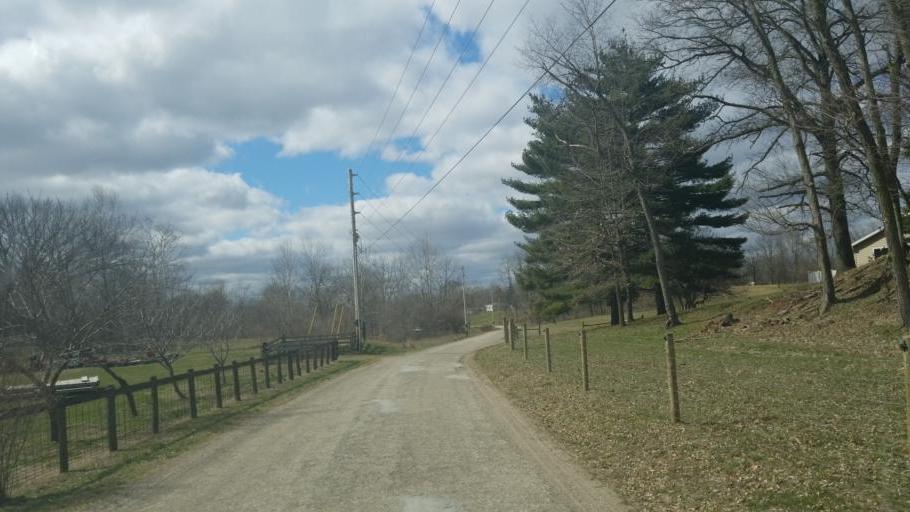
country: US
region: Indiana
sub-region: Parke County
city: Montezuma
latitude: 39.7728
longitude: -87.3245
